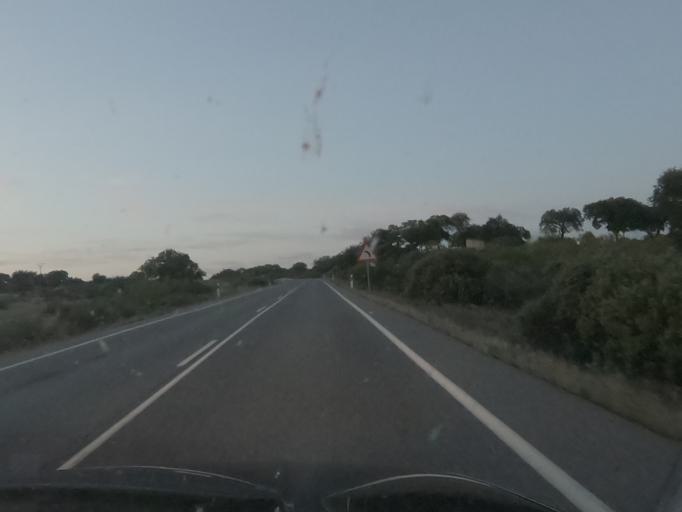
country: ES
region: Extremadura
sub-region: Provincia de Caceres
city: Alcantara
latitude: 39.7524
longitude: -6.9030
